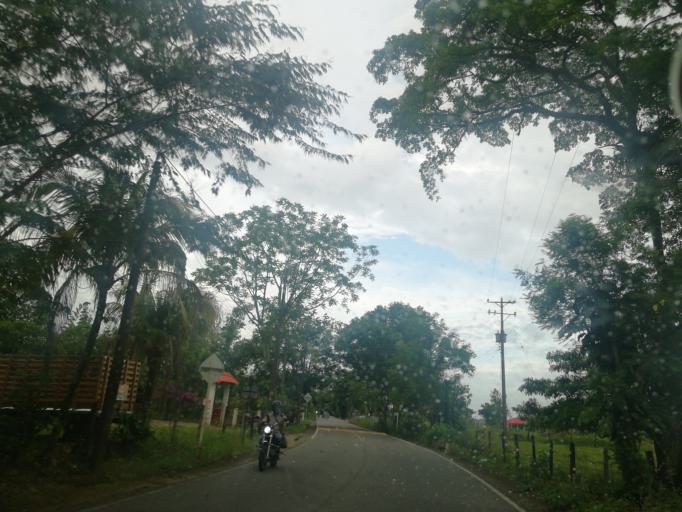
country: CO
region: Meta
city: Acacias
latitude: 3.9871
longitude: -73.7298
